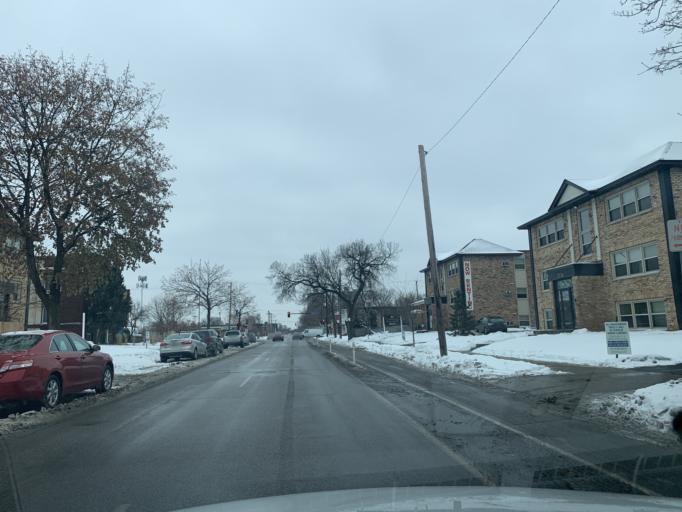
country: US
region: Minnesota
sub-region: Hennepin County
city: Minneapolis
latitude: 44.9531
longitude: -93.2797
